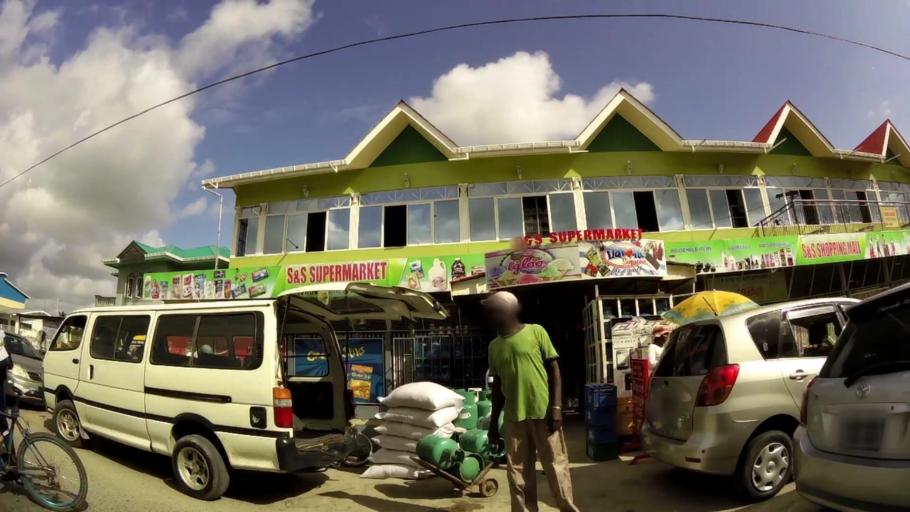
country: GY
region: Demerara-Mahaica
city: Mahaica Village
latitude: 6.6713
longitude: -57.9236
